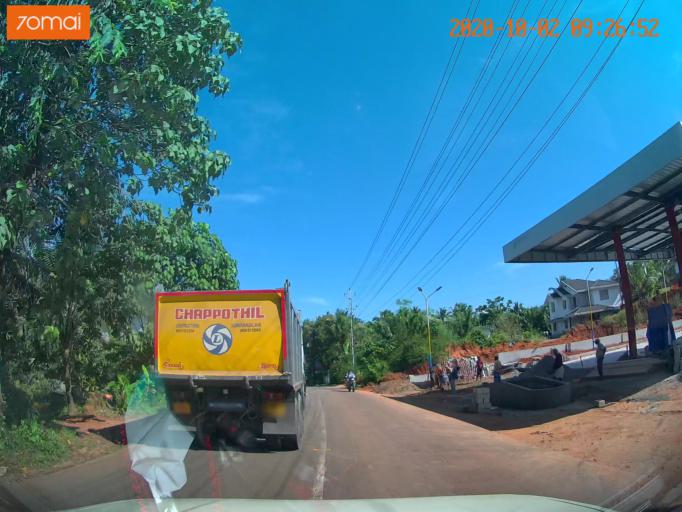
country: IN
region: Kerala
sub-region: Kozhikode
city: Naduvannur
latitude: 11.5951
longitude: 75.7656
